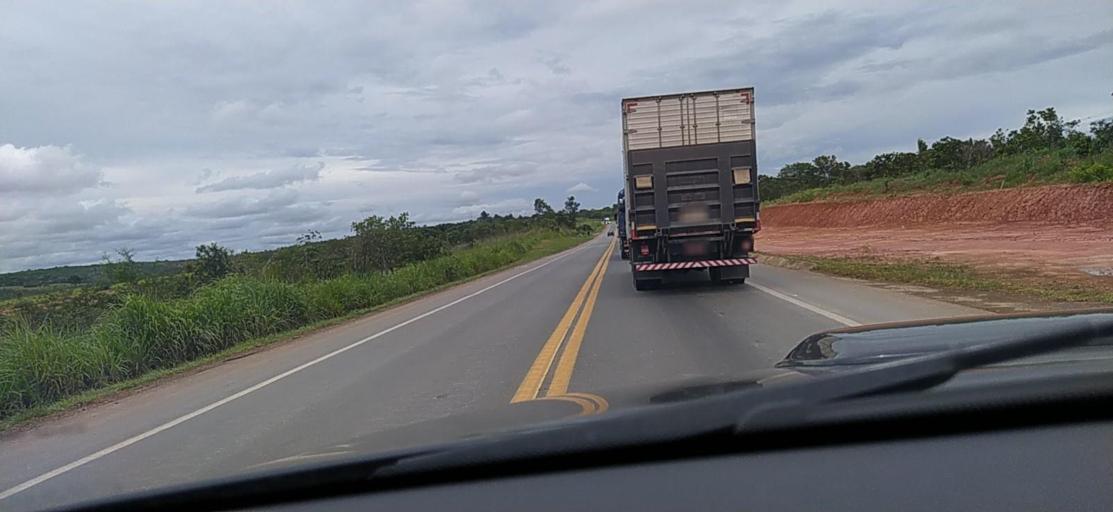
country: BR
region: Minas Gerais
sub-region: Curvelo
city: Curvelo
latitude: -18.7286
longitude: -44.4423
